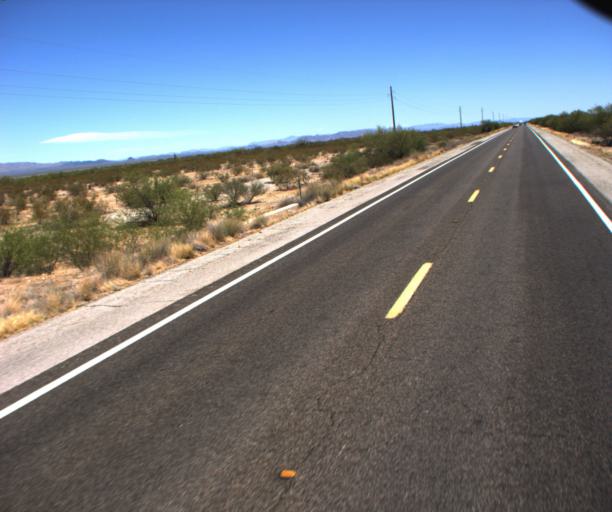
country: US
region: Arizona
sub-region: La Paz County
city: Salome
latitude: 33.8706
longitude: -113.3921
